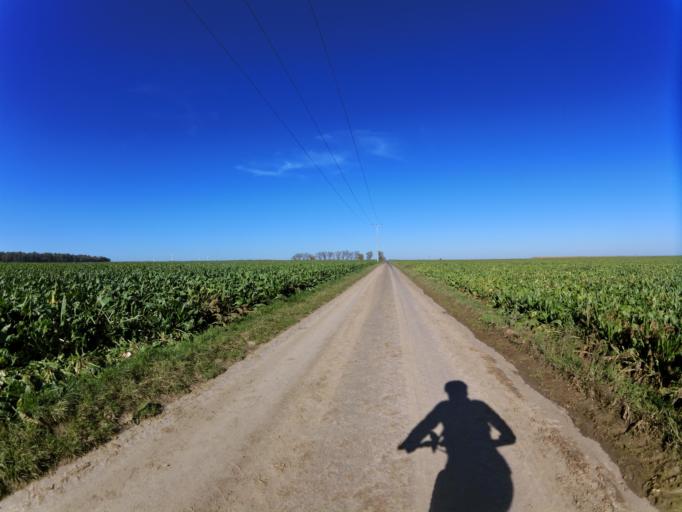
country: DE
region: Bavaria
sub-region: Regierungsbezirk Unterfranken
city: Giebelstadt
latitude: 49.6679
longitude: 9.9250
